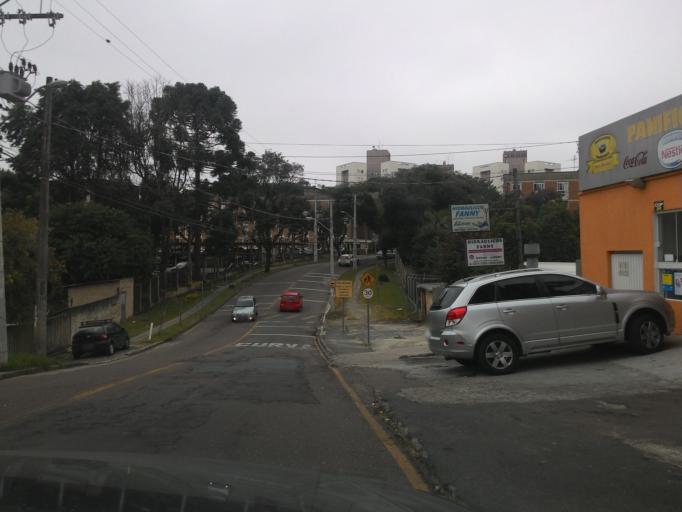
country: BR
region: Parana
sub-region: Curitiba
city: Curitiba
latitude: -25.4816
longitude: -49.2881
